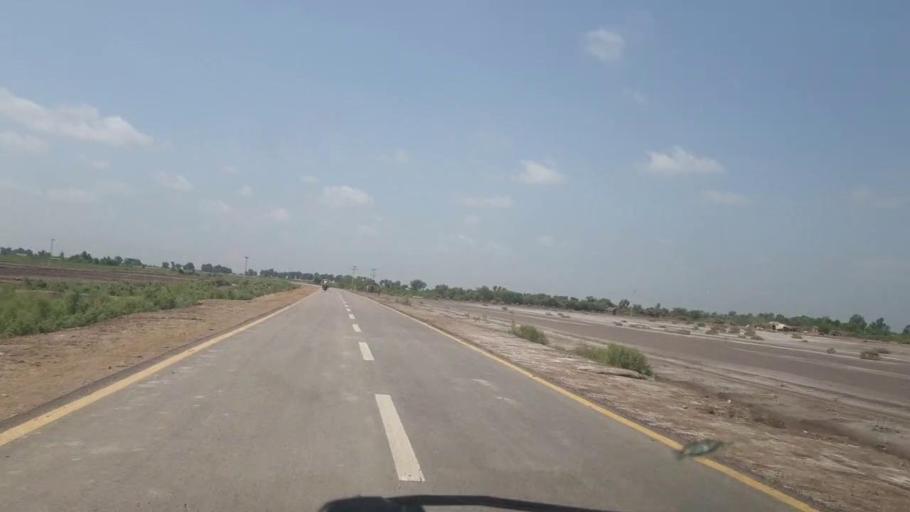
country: PK
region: Sindh
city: Berani
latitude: 25.7111
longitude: 68.9432
